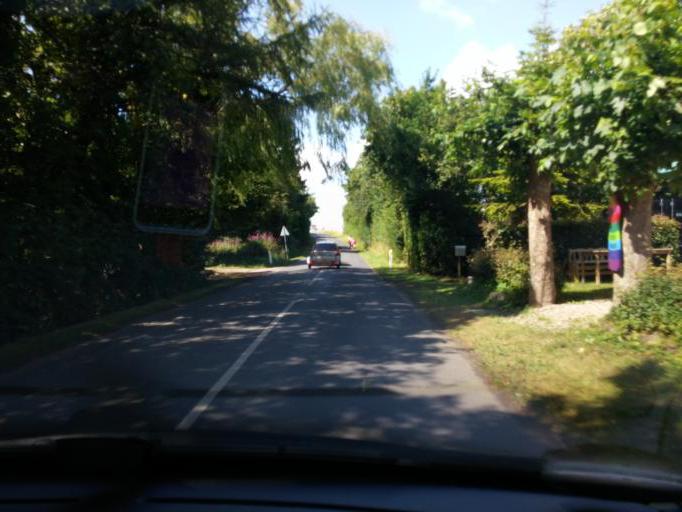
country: DK
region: South Denmark
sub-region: AEro Kommune
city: Marstal
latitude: 54.8200
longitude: 10.6394
